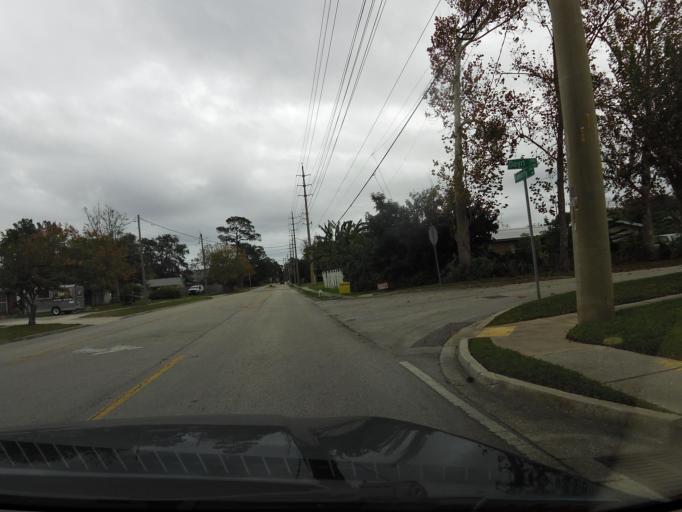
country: US
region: Florida
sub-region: Duval County
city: Jacksonville
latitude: 30.2843
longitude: -81.6076
